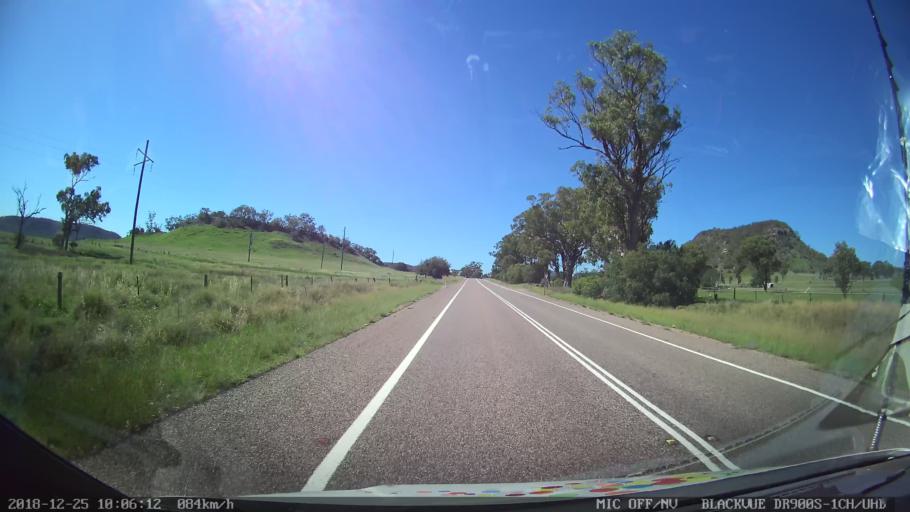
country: AU
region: New South Wales
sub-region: Upper Hunter Shire
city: Merriwa
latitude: -32.2571
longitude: 150.4891
